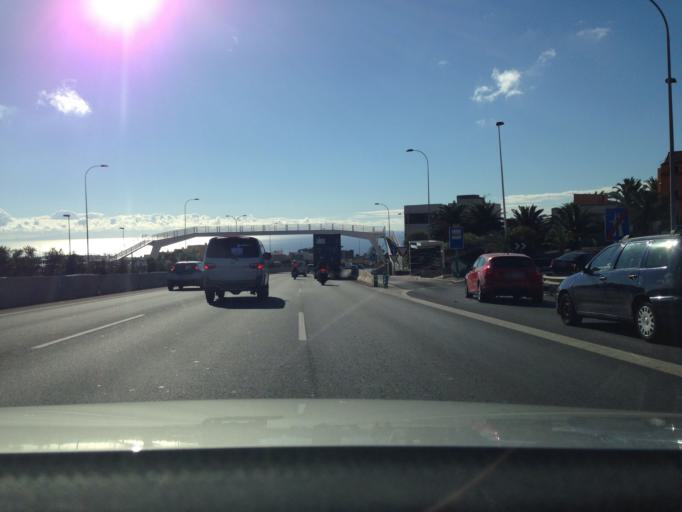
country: ES
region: Canary Islands
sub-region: Provincia de Santa Cruz de Tenerife
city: Santa Cruz de Tenerife
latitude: 28.4553
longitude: -16.2925
